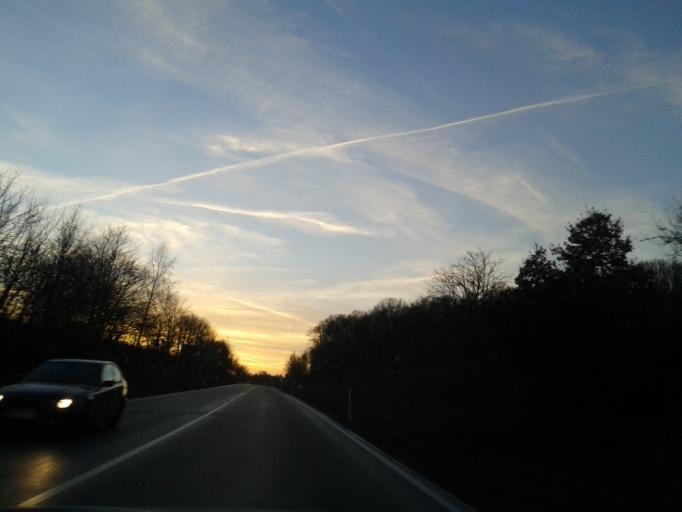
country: DE
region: Bavaria
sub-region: Regierungsbezirk Unterfranken
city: Aidhausen
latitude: 50.1138
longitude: 10.4353
